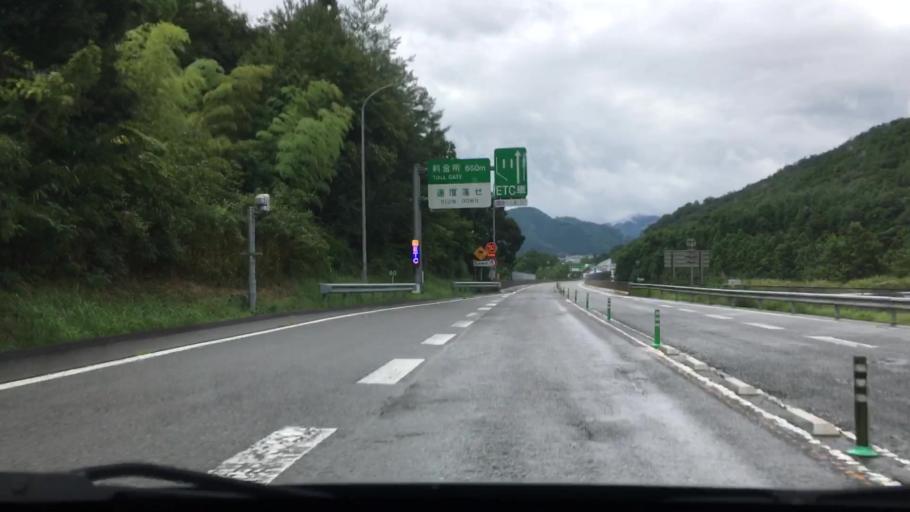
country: JP
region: Hyogo
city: Toyooka
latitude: 35.2924
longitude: 134.8246
